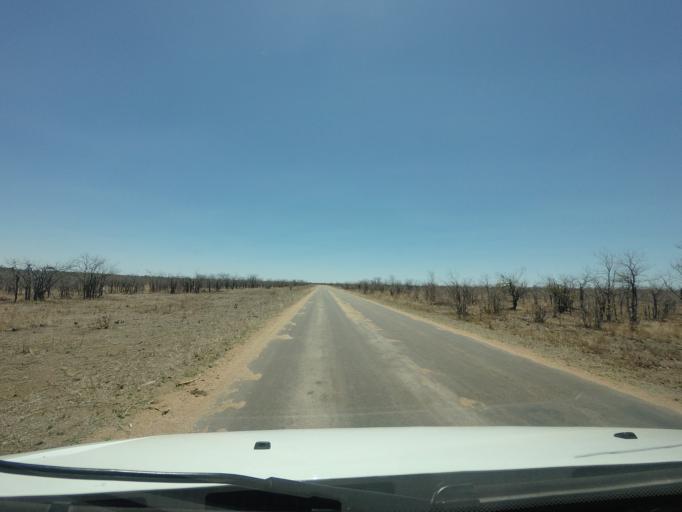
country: ZA
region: Limpopo
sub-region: Mopani District Municipality
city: Phalaborwa
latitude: -23.5705
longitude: 31.4519
